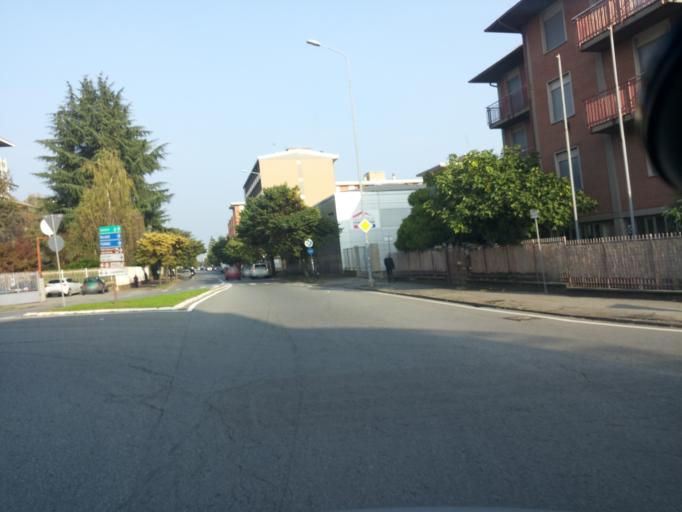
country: IT
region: Piedmont
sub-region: Provincia di Biella
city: Ponderano
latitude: 45.5517
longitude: 8.0503
